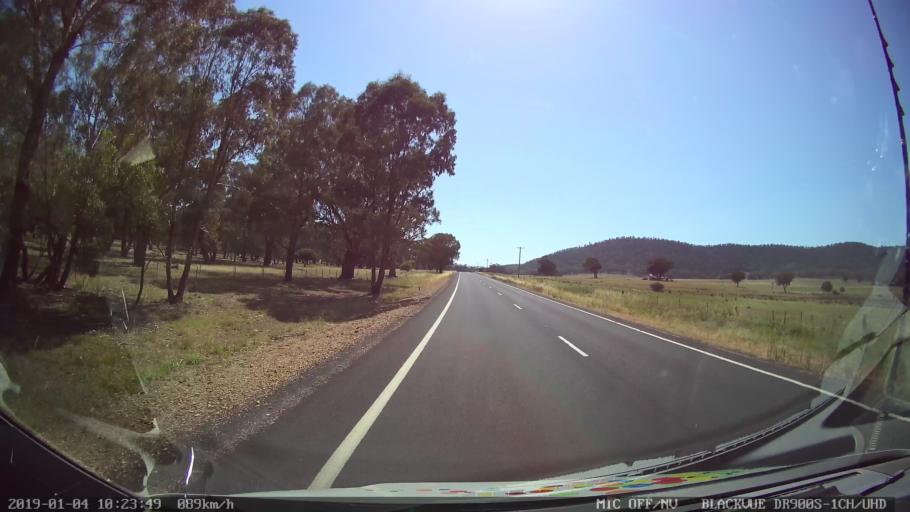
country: AU
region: New South Wales
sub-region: Cabonne
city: Canowindra
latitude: -33.3701
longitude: 148.5449
